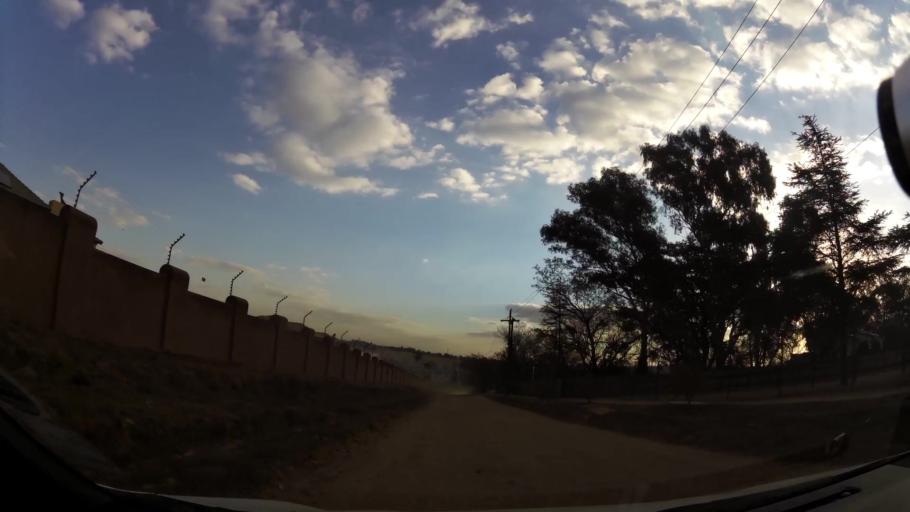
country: ZA
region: Gauteng
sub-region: City of Johannesburg Metropolitan Municipality
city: Diepsloot
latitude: -26.0052
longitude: 27.9740
